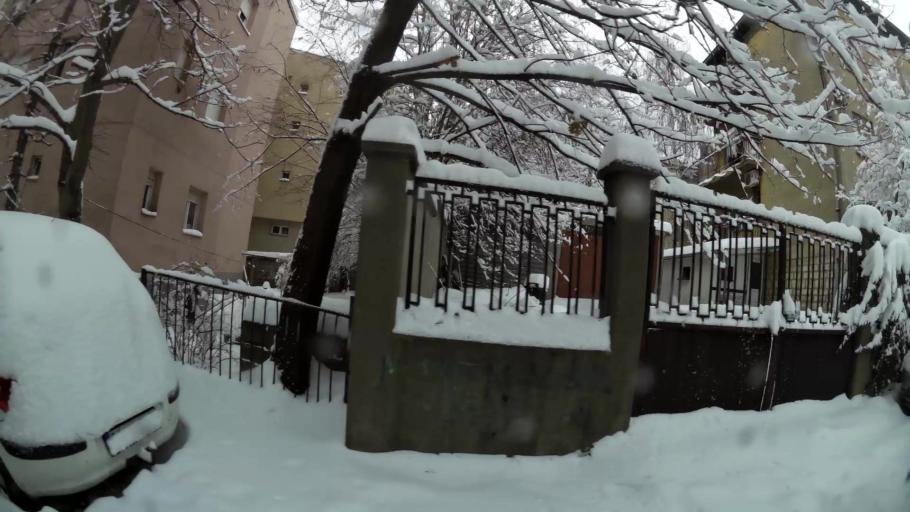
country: RS
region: Central Serbia
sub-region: Belgrade
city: Vracar
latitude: 44.7927
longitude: 20.4811
